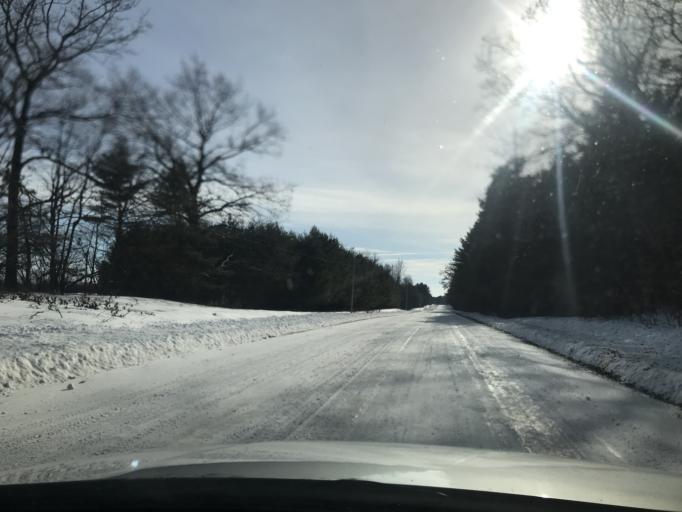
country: US
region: Wisconsin
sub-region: Oconto County
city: Gillett
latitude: 45.1319
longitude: -88.2497
